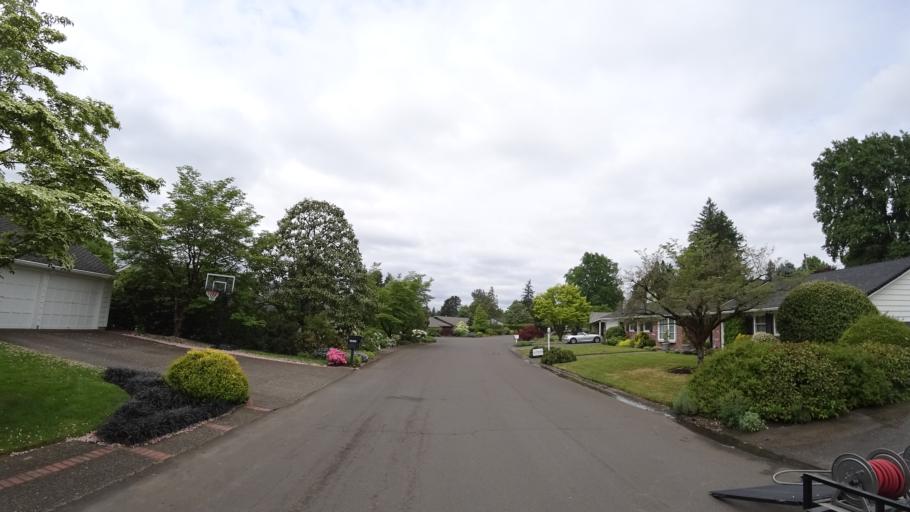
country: US
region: Oregon
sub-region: Washington County
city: Raleigh Hills
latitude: 45.4801
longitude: -122.7528
